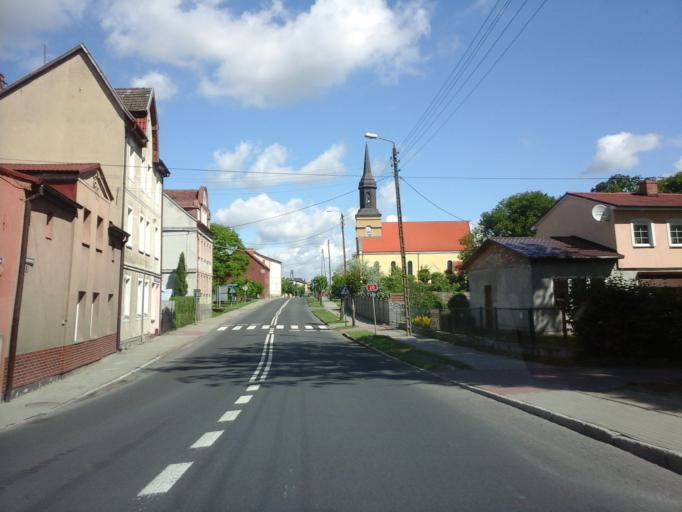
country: PL
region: West Pomeranian Voivodeship
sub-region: Powiat lobeski
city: Wegorzyno
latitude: 53.5357
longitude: 15.5582
